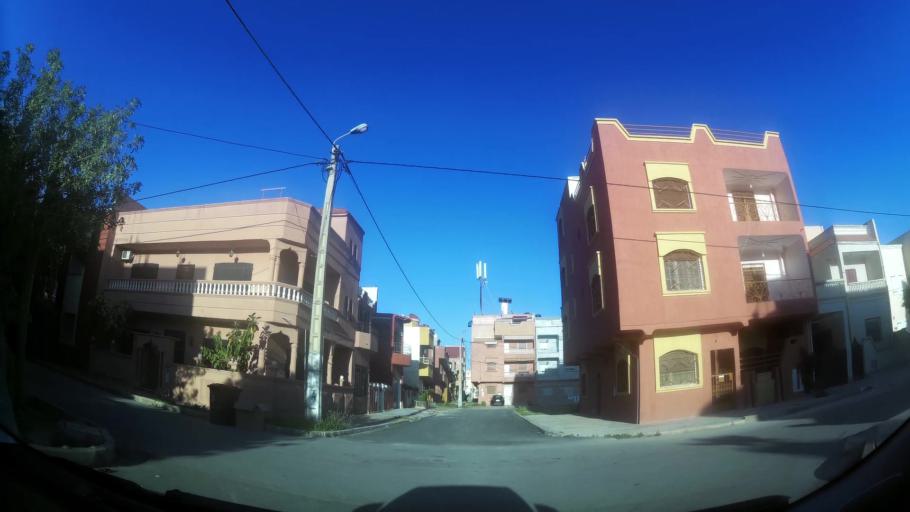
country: MA
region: Oriental
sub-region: Berkane-Taourirt
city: Madagh
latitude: 35.0850
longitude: -2.2377
